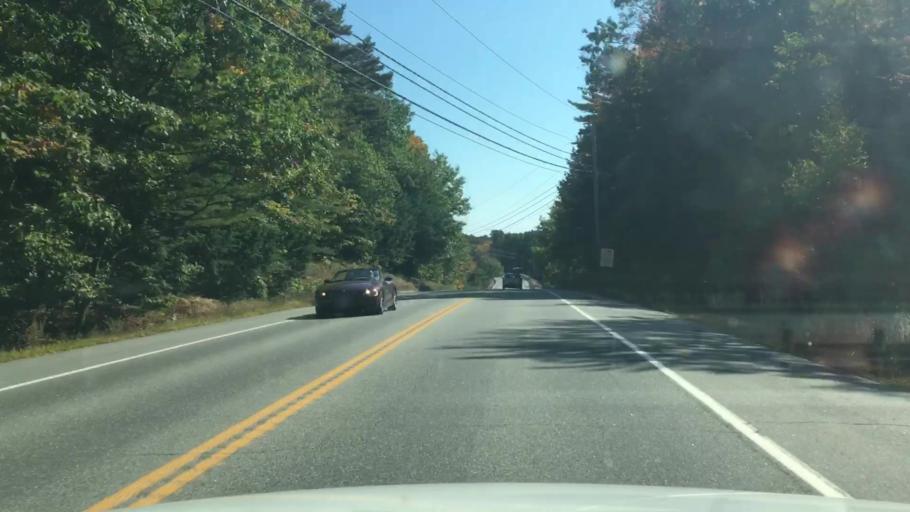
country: US
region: Maine
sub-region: Androscoggin County
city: Lisbon Falls
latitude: 43.9665
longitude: -70.0189
